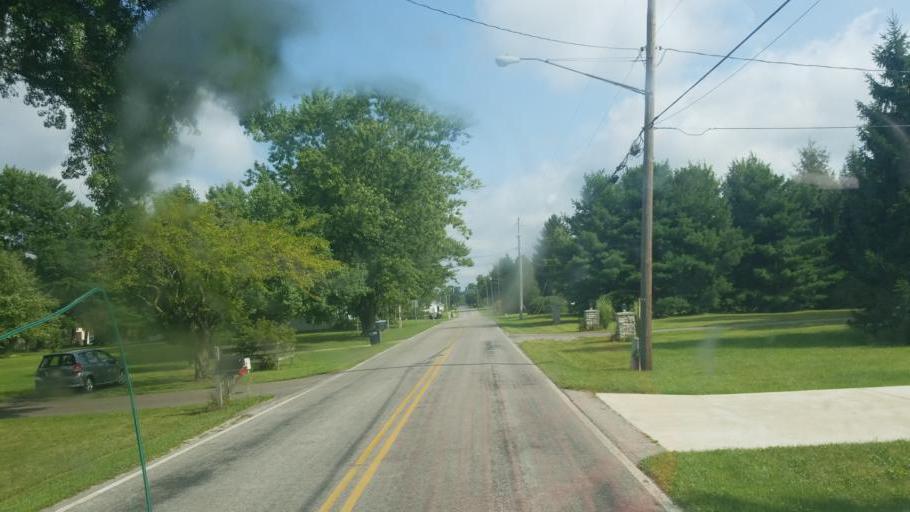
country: US
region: Ohio
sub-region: Morrow County
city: Cardington
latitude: 40.5806
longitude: -82.9967
